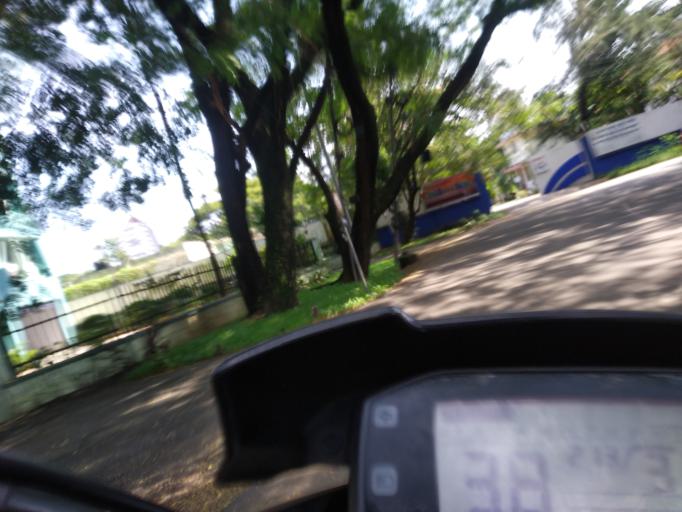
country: IN
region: Kerala
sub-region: Ernakulam
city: Cochin
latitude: 9.9690
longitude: 76.2936
